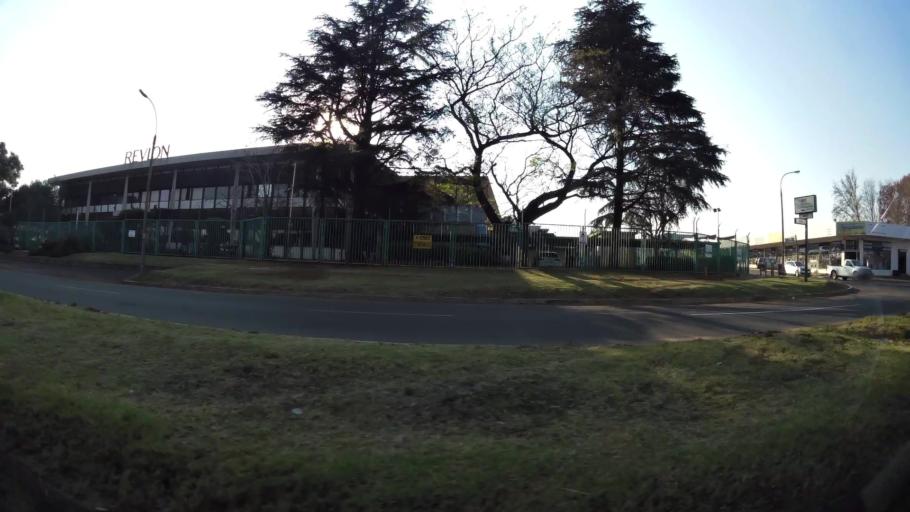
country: ZA
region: Gauteng
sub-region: City of Johannesburg Metropolitan Municipality
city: Modderfontein
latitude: -26.1421
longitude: 28.1979
